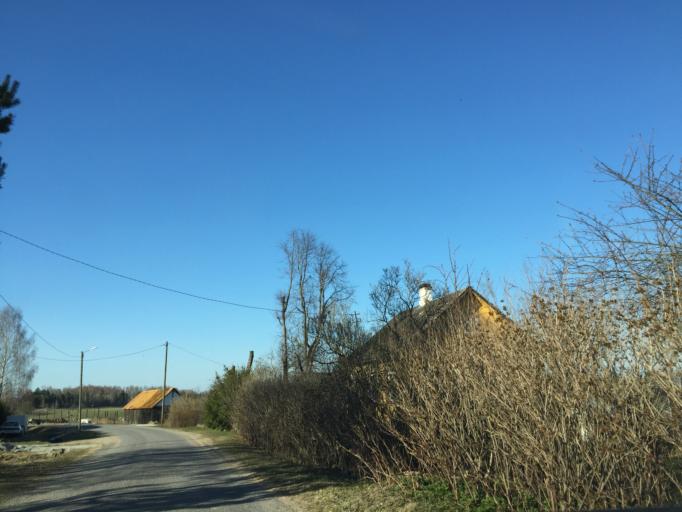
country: EE
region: Ida-Virumaa
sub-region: Sillamaee linn
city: Sillamae
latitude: 59.1246
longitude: 27.8033
